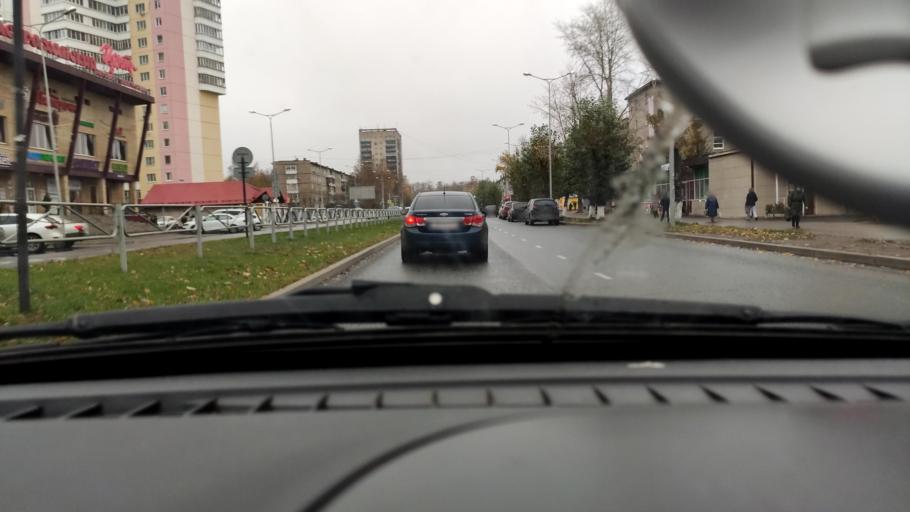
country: RU
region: Perm
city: Kultayevo
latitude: 58.0051
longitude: 55.9514
